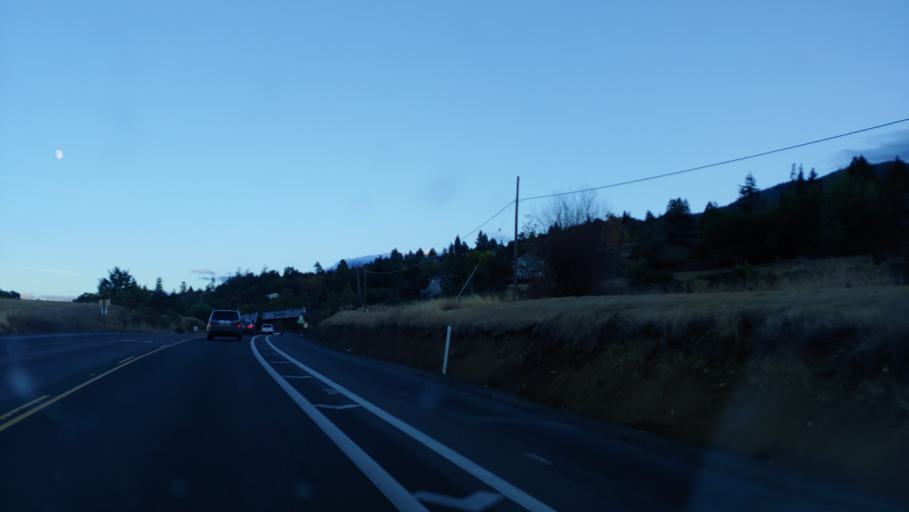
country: US
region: Oregon
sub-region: Jackson County
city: Ashland
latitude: 42.2155
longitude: -122.7321
